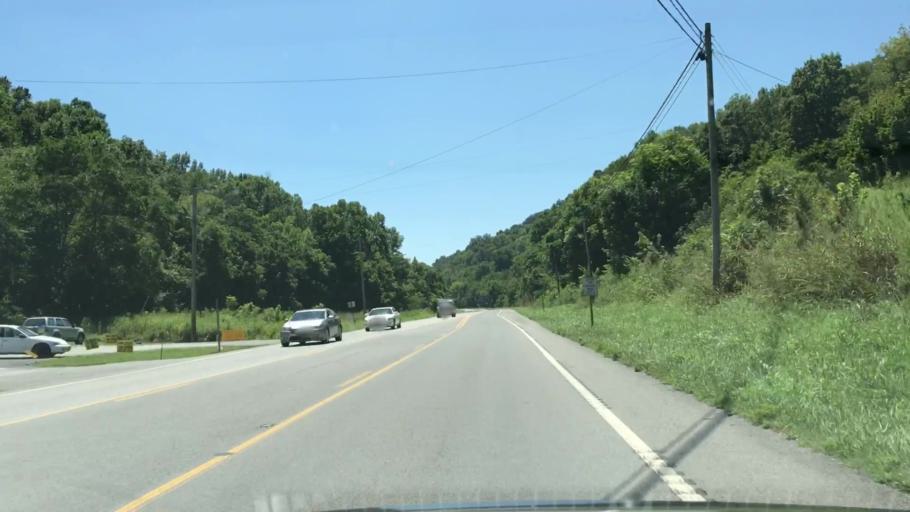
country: US
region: Tennessee
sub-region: Jackson County
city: Gainesboro
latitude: 36.3364
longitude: -85.6575
